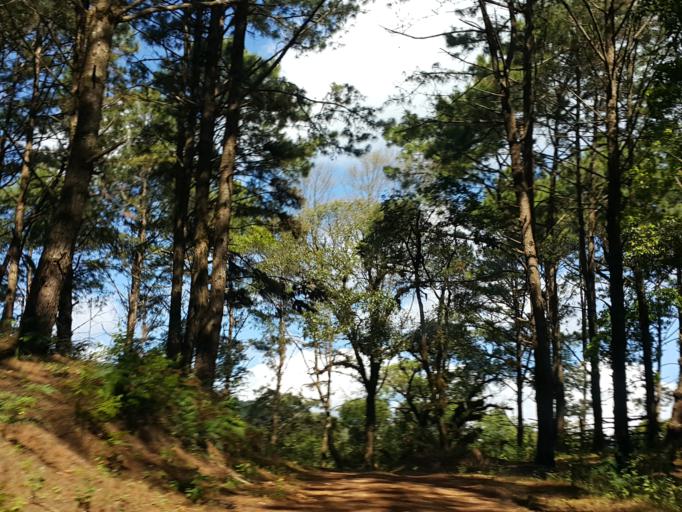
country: TH
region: Chiang Mai
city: Wiang Haeng
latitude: 19.5400
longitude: 98.8143
